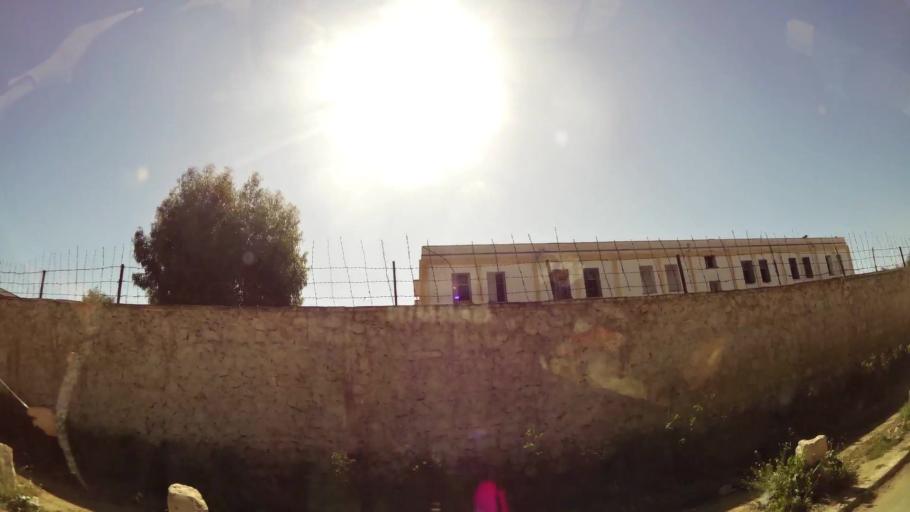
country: MA
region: Meknes-Tafilalet
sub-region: Meknes
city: Meknes
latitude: 33.8911
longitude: -5.5305
